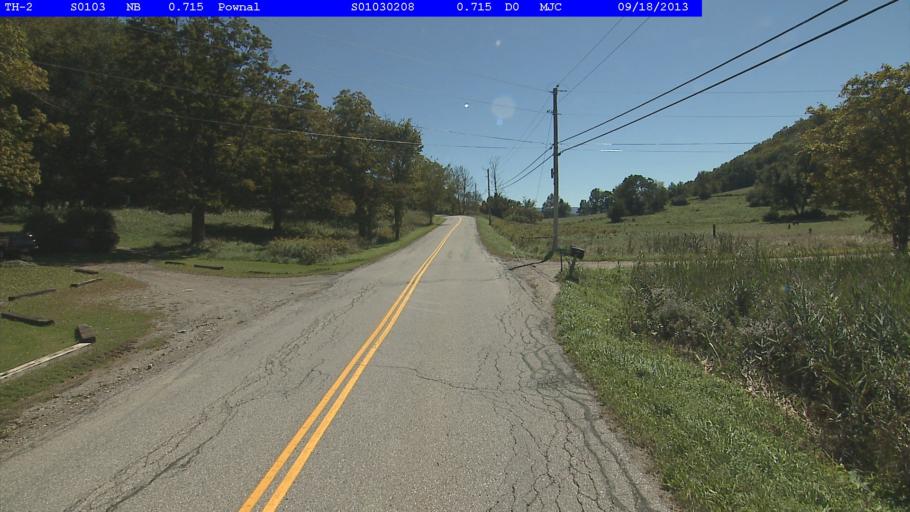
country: US
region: Vermont
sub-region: Bennington County
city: Bennington
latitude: 42.8037
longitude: -73.2551
